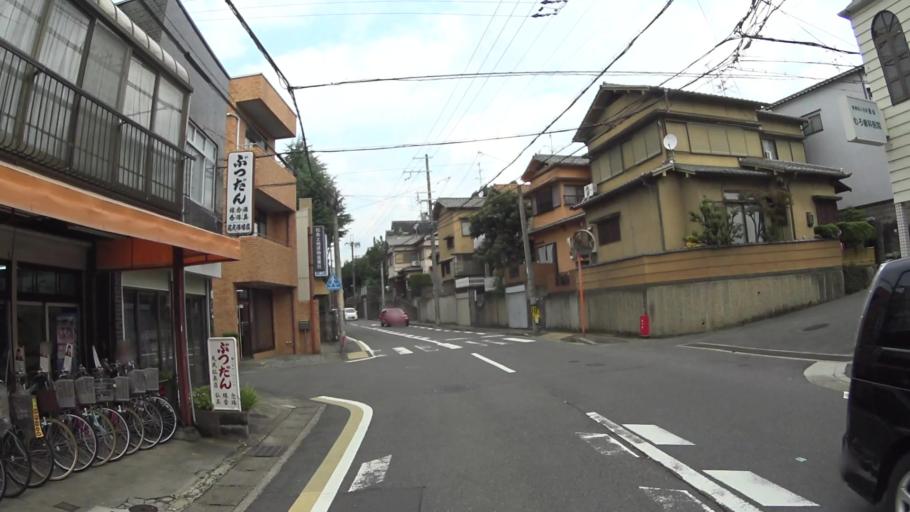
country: JP
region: Kyoto
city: Muko
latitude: 35.0109
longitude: 135.7084
